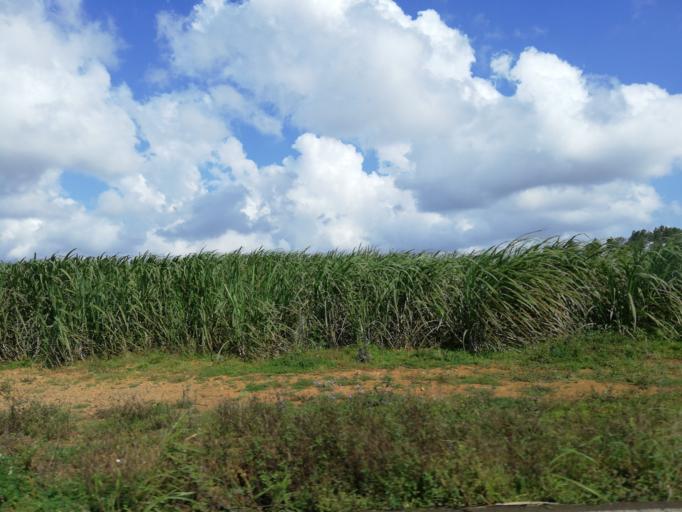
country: MU
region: Pamplemousses
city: Creve Coeur
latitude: -20.2118
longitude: 57.5577
